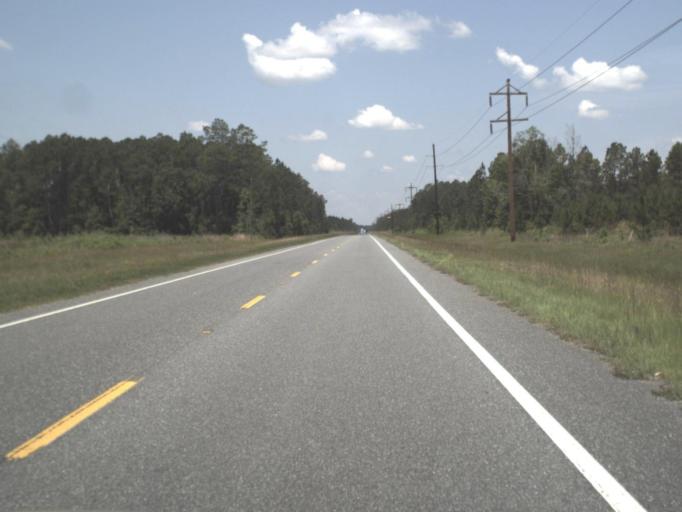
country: US
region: Florida
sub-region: Bradford County
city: Starke
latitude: 29.9744
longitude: -82.2193
